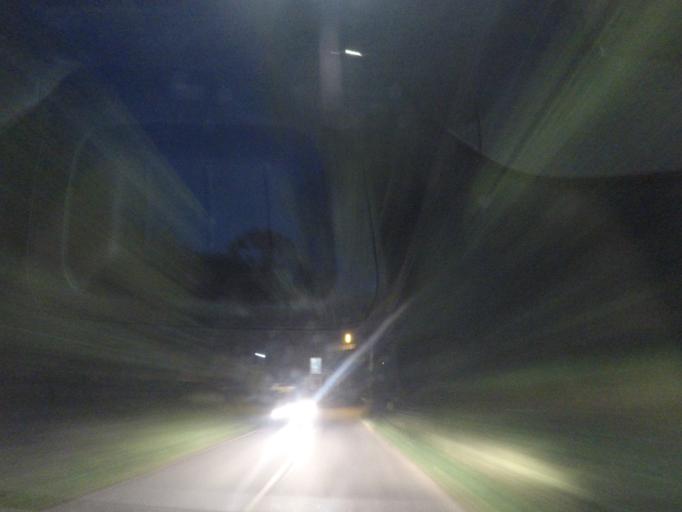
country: BR
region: Parana
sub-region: Curitiba
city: Curitiba
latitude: -25.4205
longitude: -49.3139
